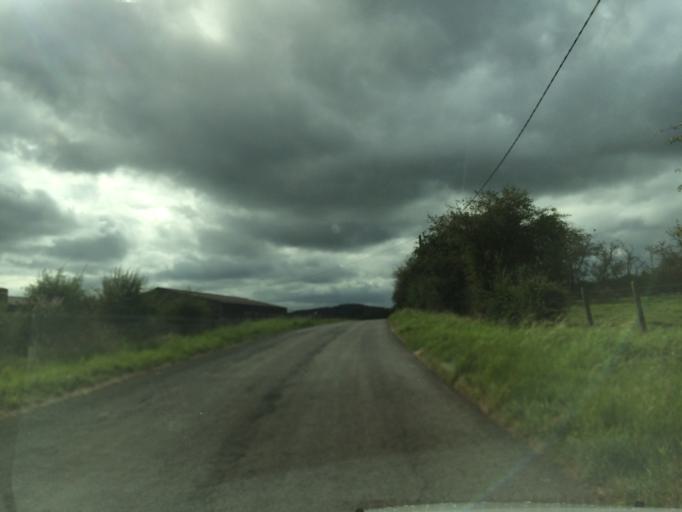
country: BE
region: Wallonia
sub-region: Province du Luxembourg
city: Chiny
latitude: 49.6944
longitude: 5.3644
